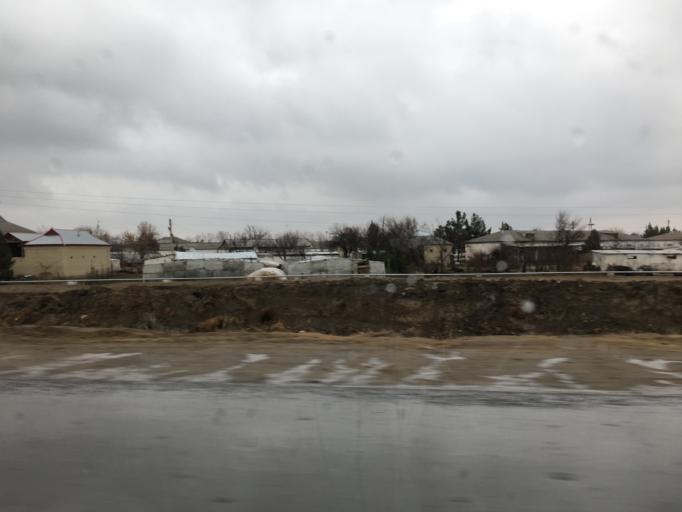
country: TM
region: Mary
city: Mary
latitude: 37.5354
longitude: 61.8863
